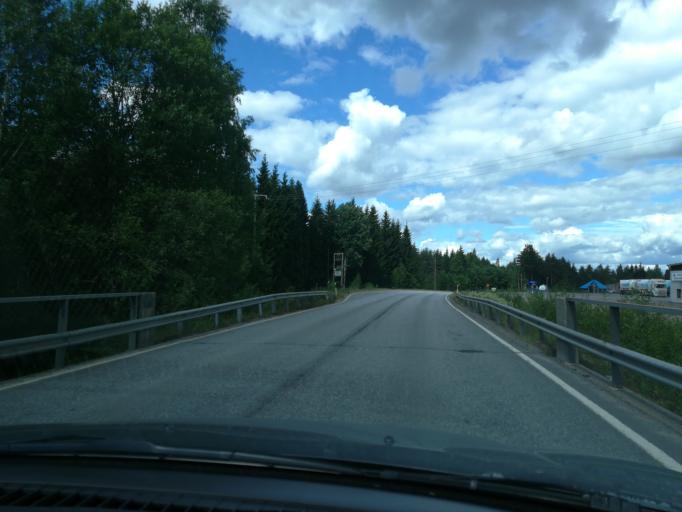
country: FI
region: Southern Savonia
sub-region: Mikkeli
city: Maentyharju
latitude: 61.4000
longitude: 26.8975
